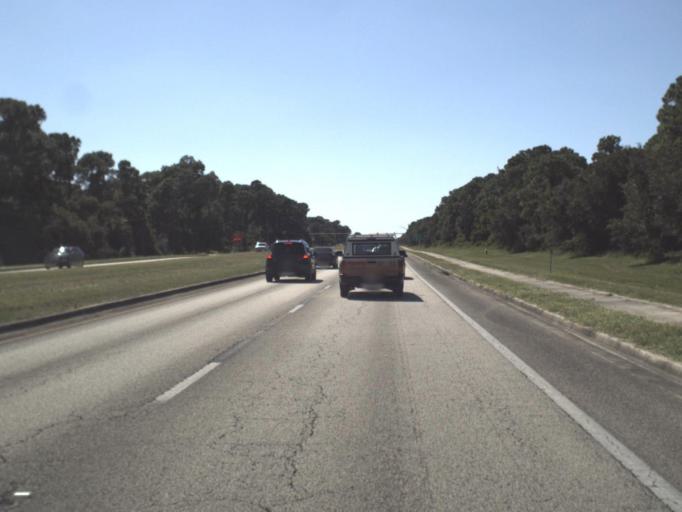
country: US
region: Florida
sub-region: Sarasota County
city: North Port
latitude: 27.0056
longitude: -82.1676
